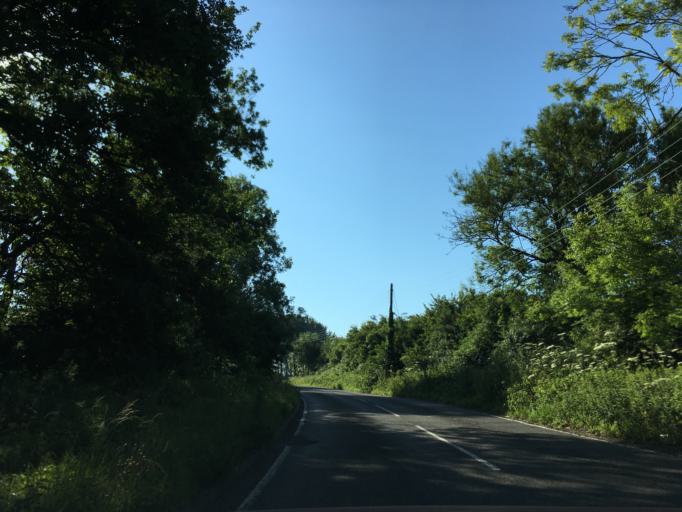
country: GB
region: England
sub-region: South Gloucestershire
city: Siston
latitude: 51.4655
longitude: -2.4677
